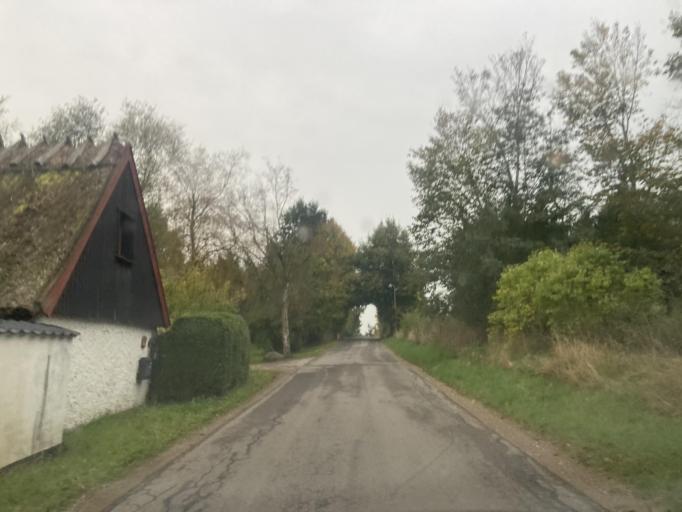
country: DK
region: Capital Region
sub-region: Egedal Kommune
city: Vekso
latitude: 55.7176
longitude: 12.2160
